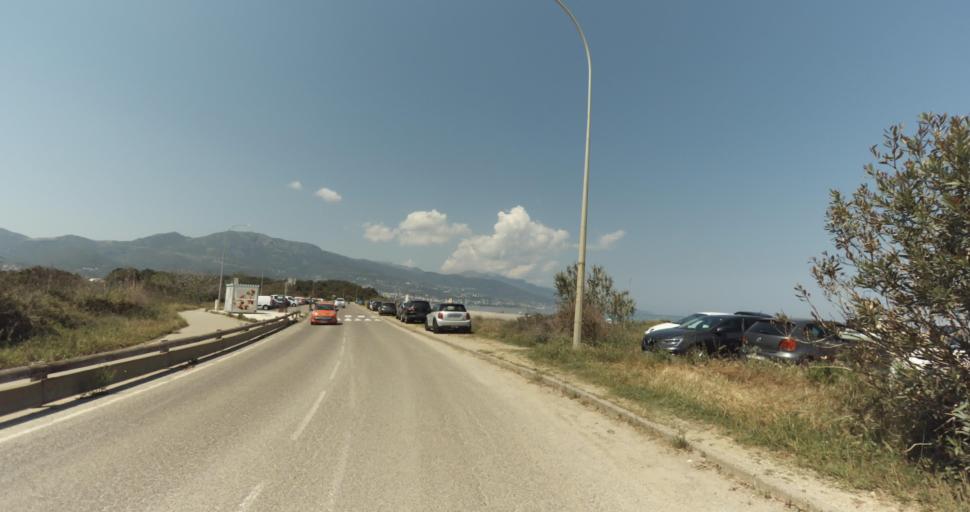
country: FR
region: Corsica
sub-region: Departement de la Haute-Corse
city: Biguglia
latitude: 42.6408
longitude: 9.4610
